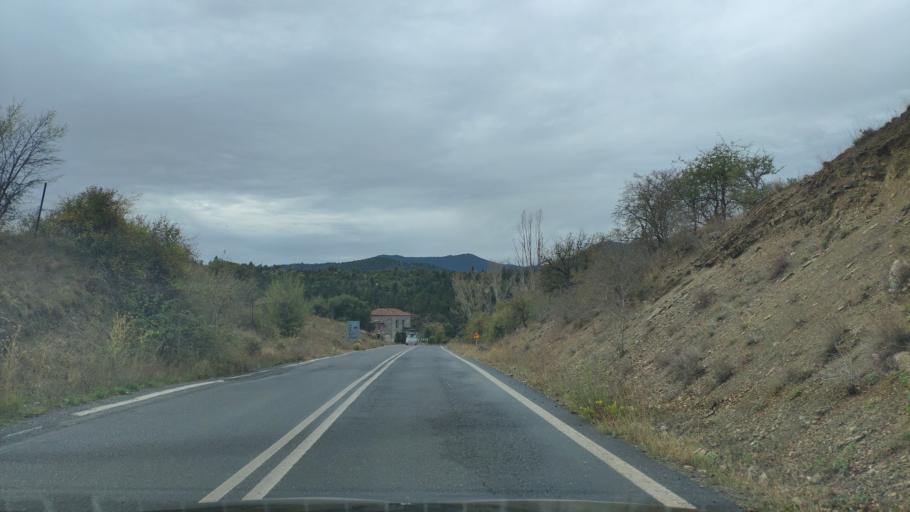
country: GR
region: Peloponnese
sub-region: Nomos Arkadias
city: Dimitsana
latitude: 37.6525
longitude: 22.1875
